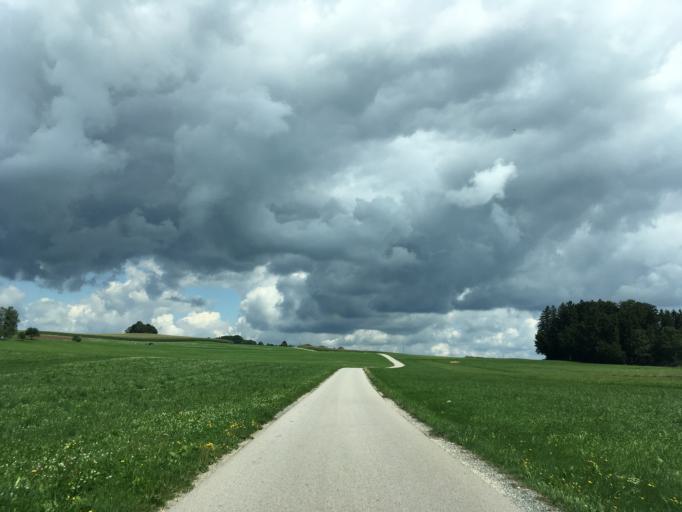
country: DE
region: Bavaria
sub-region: Upper Bavaria
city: Amerang
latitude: 47.9885
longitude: 12.3401
